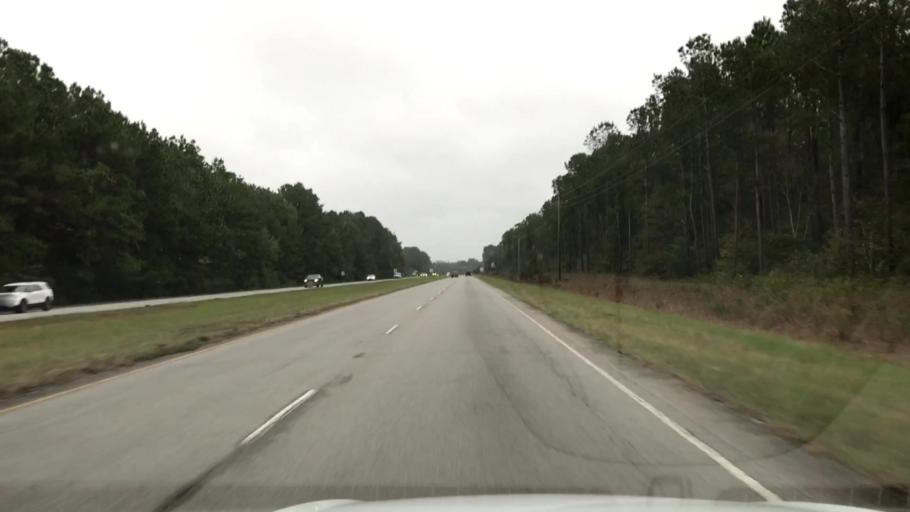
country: US
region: South Carolina
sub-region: Charleston County
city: Awendaw
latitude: 33.0200
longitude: -79.6325
